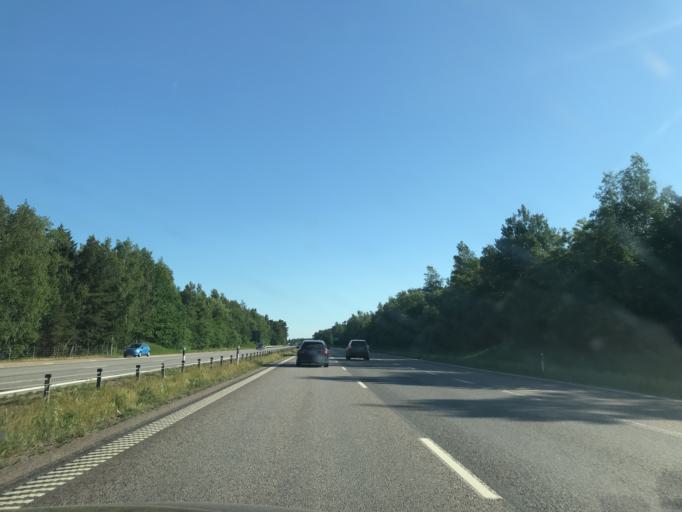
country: SE
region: Halland
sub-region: Laholms Kommun
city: Mellbystrand
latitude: 56.5081
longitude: 12.9614
